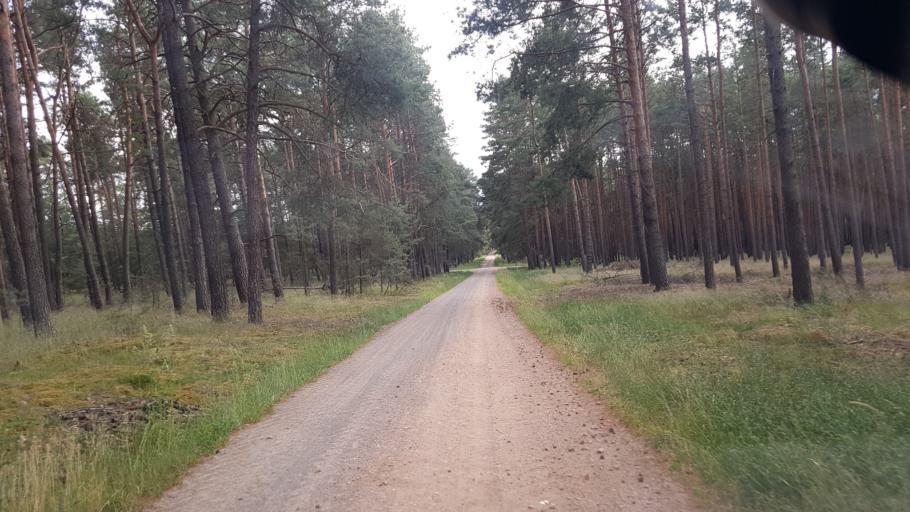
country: DE
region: Brandenburg
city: Herzberg
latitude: 51.7320
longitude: 13.2726
